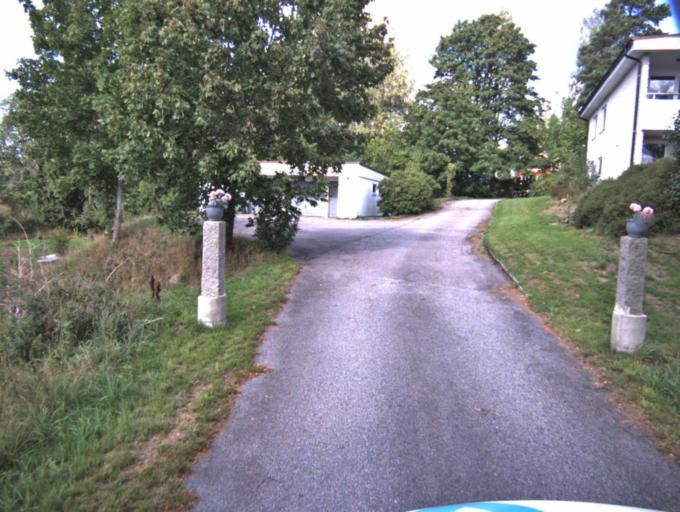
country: SE
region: Vaestra Goetaland
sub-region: Ulricehamns Kommun
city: Ulricehamn
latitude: 57.9338
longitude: 13.4958
